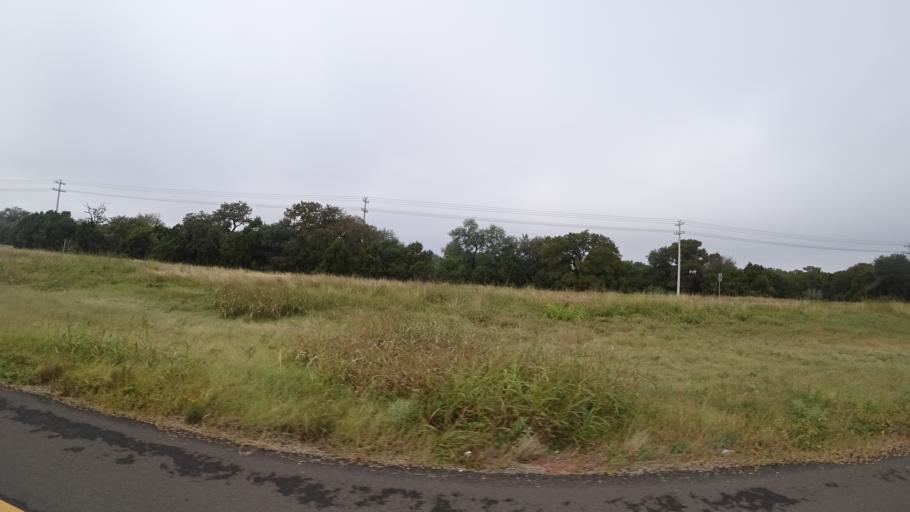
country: US
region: Texas
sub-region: Travis County
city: Shady Hollow
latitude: 30.1867
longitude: -97.8776
